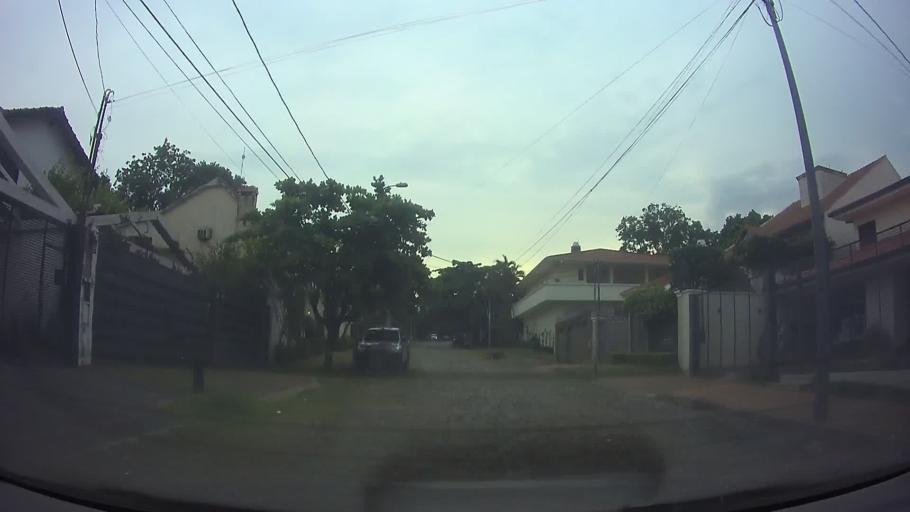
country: PY
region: Asuncion
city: Asuncion
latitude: -25.2760
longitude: -57.5692
